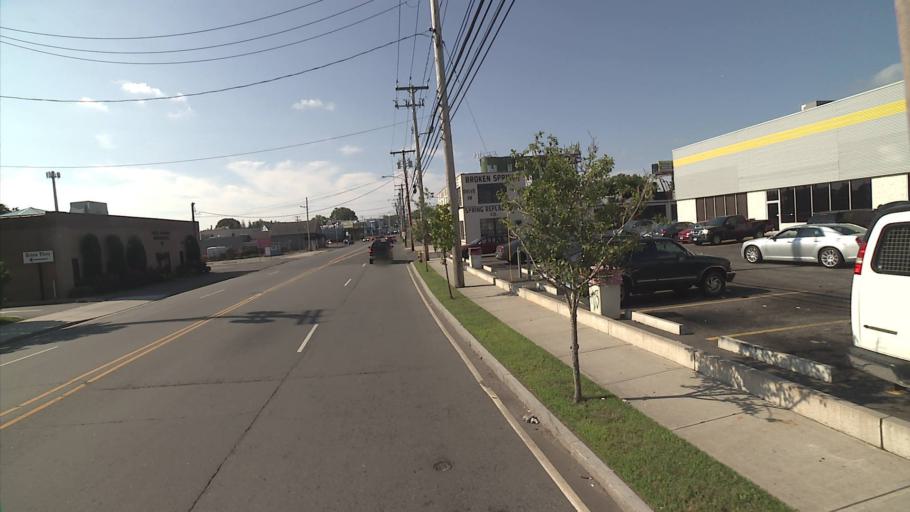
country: US
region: Connecticut
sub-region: Fairfield County
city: Bridgeport
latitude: 41.1997
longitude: -73.1924
